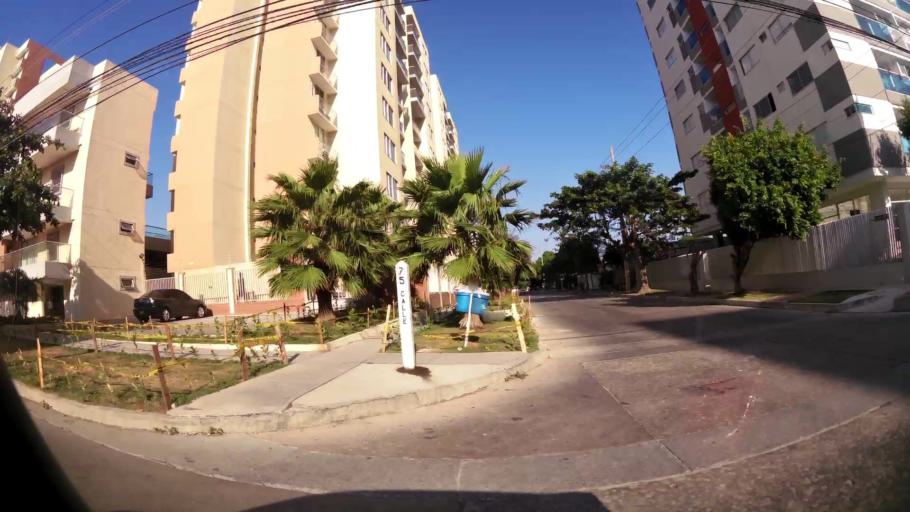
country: CO
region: Atlantico
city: Barranquilla
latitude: 11.0082
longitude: -74.7965
